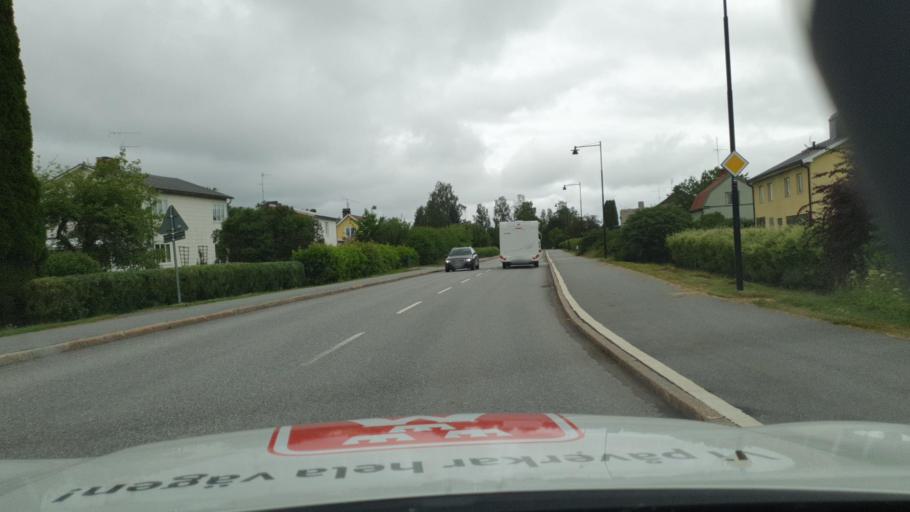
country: SE
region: Vaermland
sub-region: Karlstads Kommun
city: Valberg
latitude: 59.3909
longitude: 13.1908
